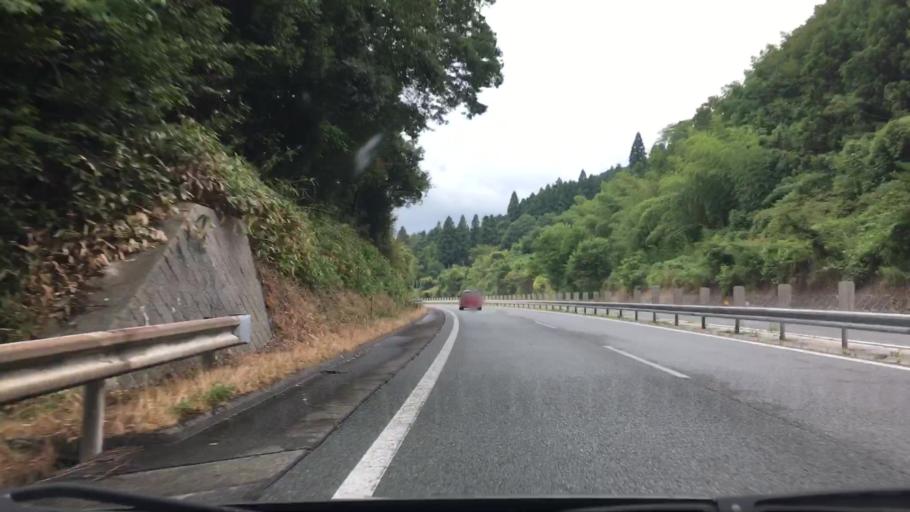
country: JP
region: Okayama
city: Niimi
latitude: 34.9564
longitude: 133.3292
